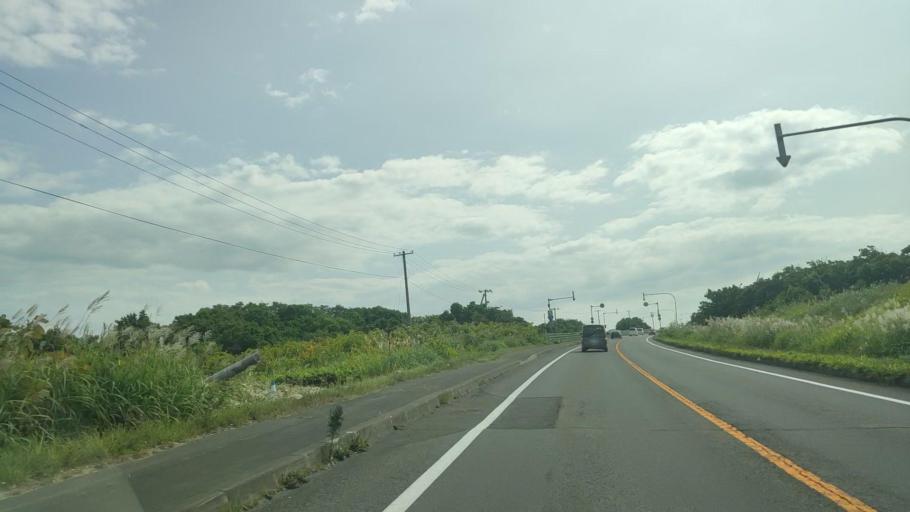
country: JP
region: Hokkaido
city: Rumoi
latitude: 44.3294
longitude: 141.6780
